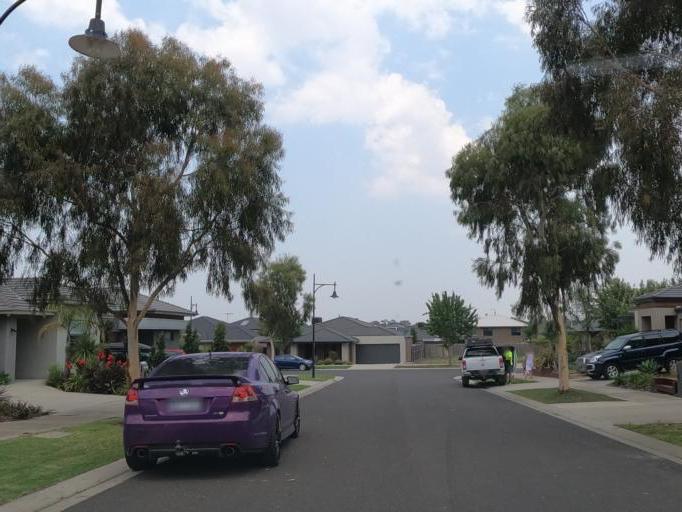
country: AU
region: Victoria
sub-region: Hume
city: Greenvale
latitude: -37.6250
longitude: 144.8883
